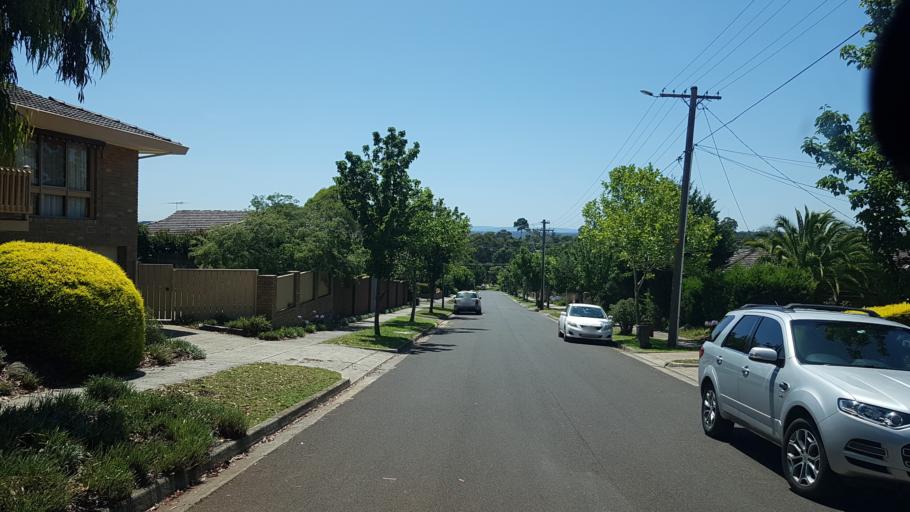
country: AU
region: Victoria
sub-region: Manningham
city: Bulleen
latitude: -37.7654
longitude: 145.0988
